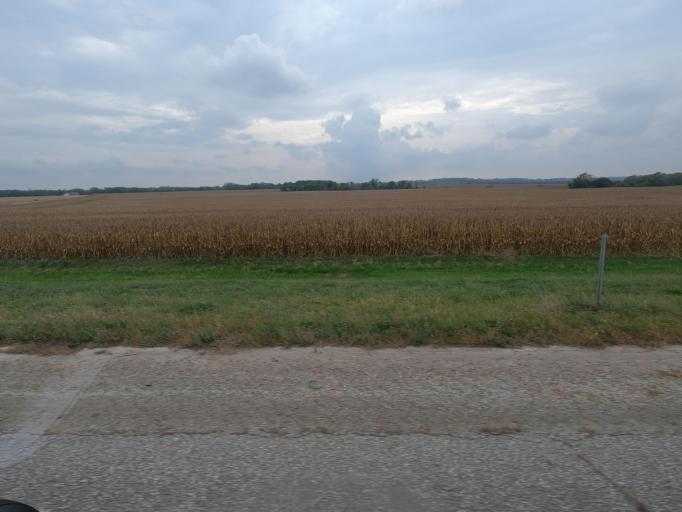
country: US
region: Iowa
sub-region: Wapello County
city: Eddyville
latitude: 41.1317
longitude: -92.5739
